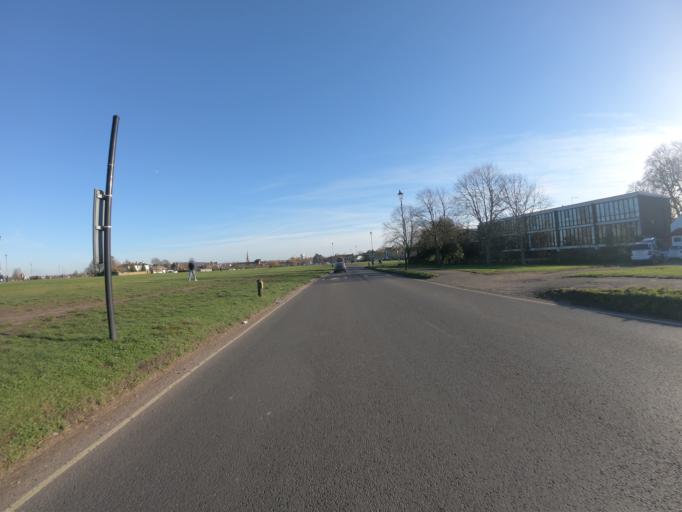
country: GB
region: England
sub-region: Greater London
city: Blackheath
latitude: 51.4696
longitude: -0.0010
